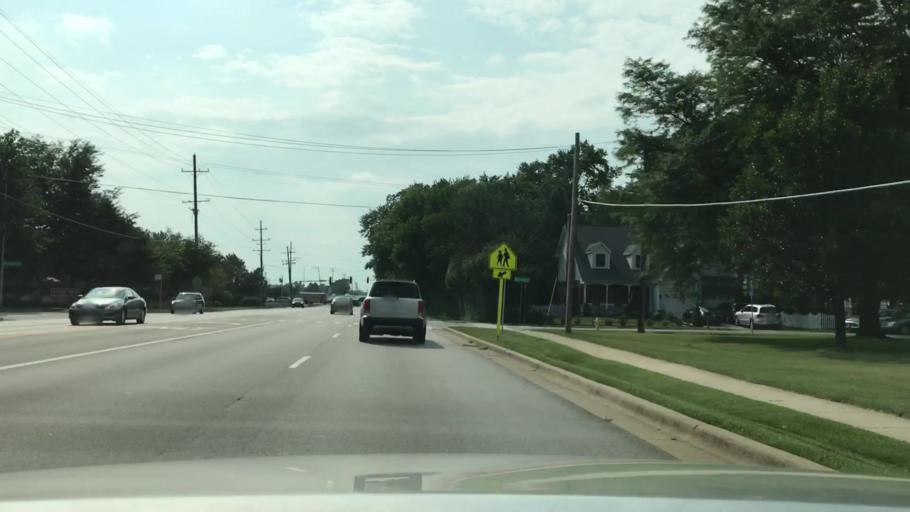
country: US
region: Illinois
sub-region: DuPage County
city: Woodridge
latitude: 41.7727
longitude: -88.0288
